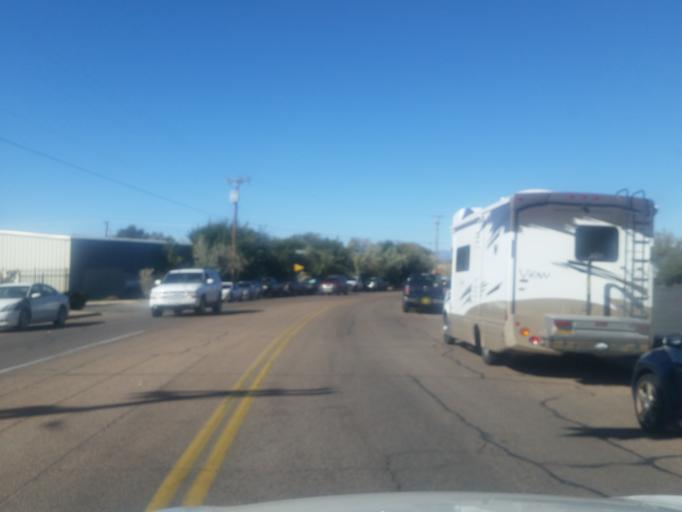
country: US
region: New Mexico
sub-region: Santa Fe County
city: Santa Fe
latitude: 35.6614
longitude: -105.9634
